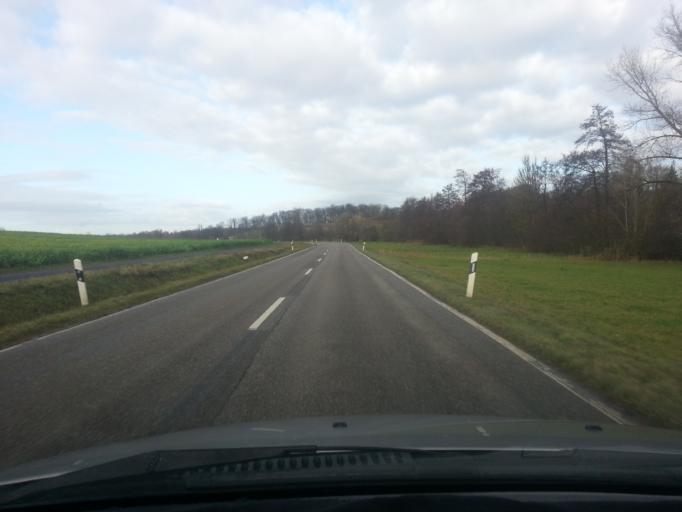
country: DE
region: Baden-Wuerttemberg
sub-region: Regierungsbezirk Stuttgart
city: Eppingen
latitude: 49.1500
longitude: 8.8930
